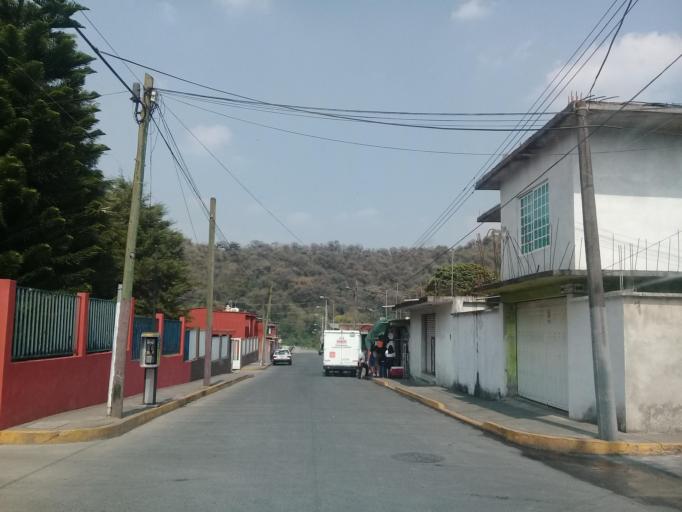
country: MX
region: Veracruz
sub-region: Mariano Escobedo
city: Palmira
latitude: 18.8781
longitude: -97.1051
